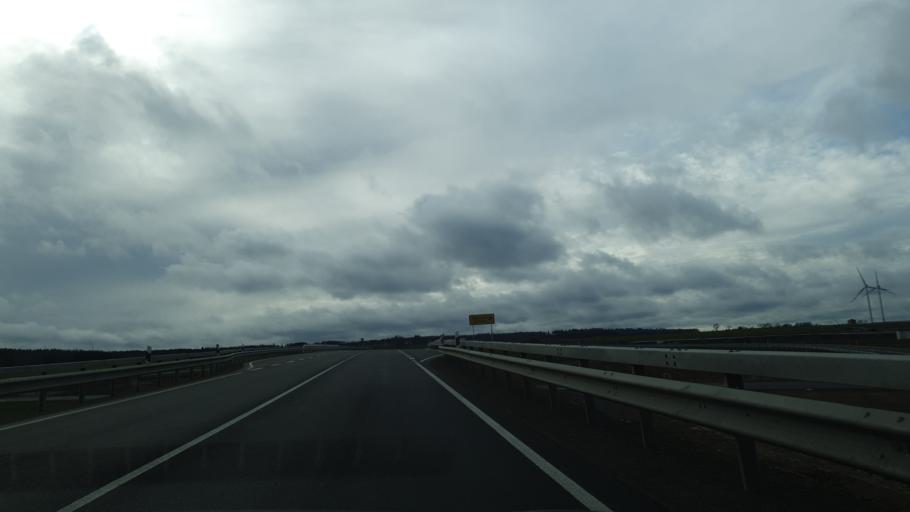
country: DE
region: Rheinland-Pfalz
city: Braunshorn
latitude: 50.0858
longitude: 7.5007
